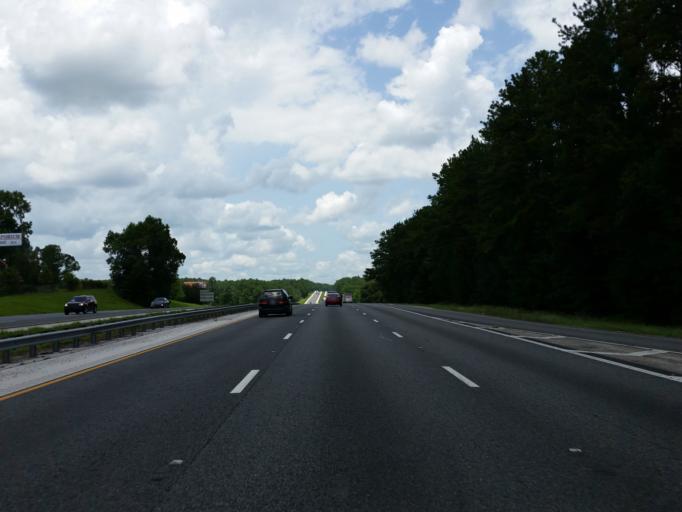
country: US
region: Florida
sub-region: Marion County
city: Citra
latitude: 29.4095
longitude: -82.2494
